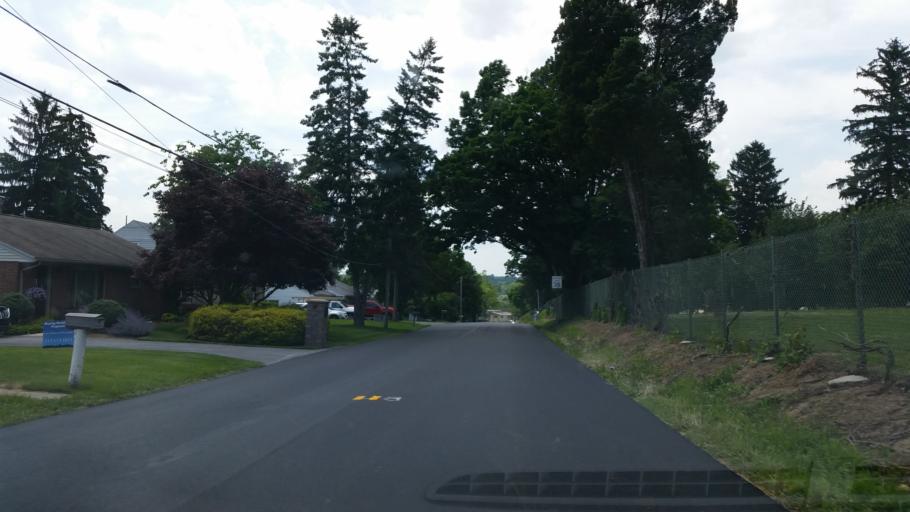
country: US
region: Pennsylvania
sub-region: Dauphin County
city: Steelton
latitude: 40.2122
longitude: -76.8553
